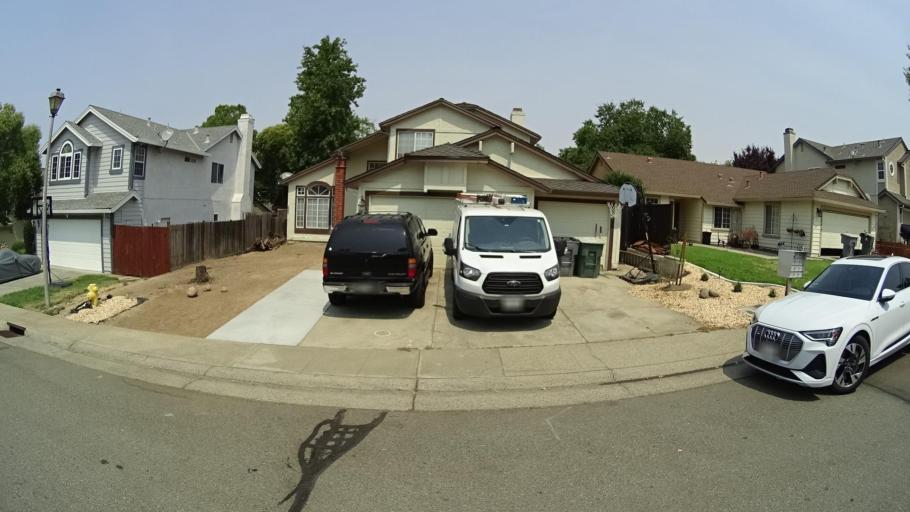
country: US
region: California
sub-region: Placer County
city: Rocklin
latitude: 38.8007
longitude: -121.2596
